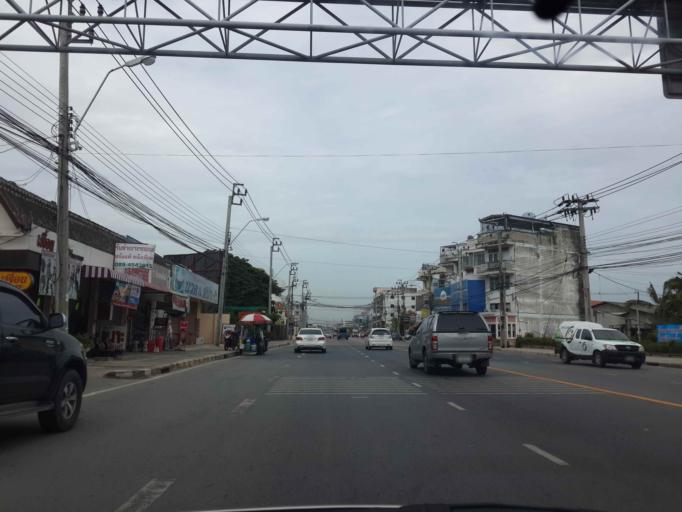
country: TH
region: Bangkok
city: Bang Khen
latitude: 13.8812
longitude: 100.6518
